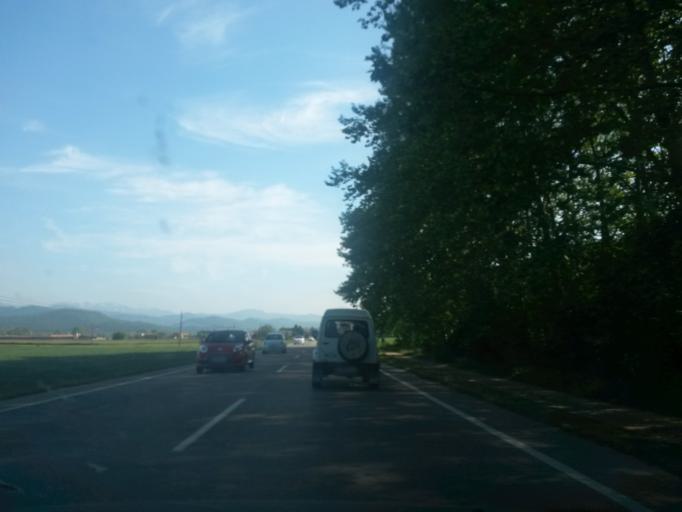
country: ES
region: Catalonia
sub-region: Provincia de Girona
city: Bas
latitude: 42.1345
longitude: 2.4531
